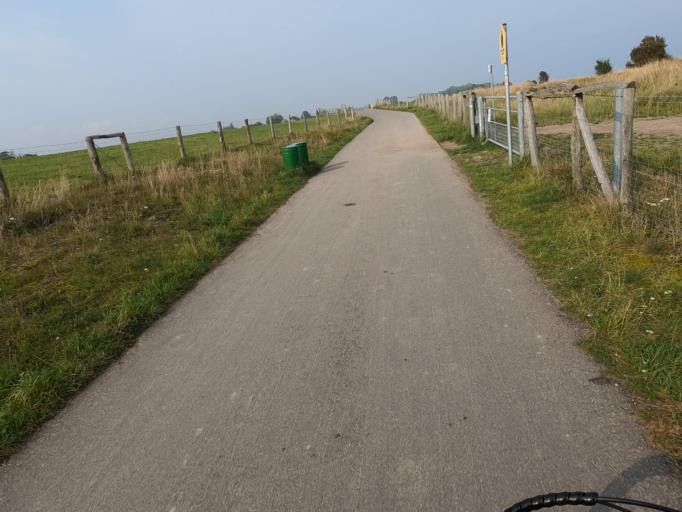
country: DE
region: Schleswig-Holstein
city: Dahme
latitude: 54.2592
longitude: 11.0812
